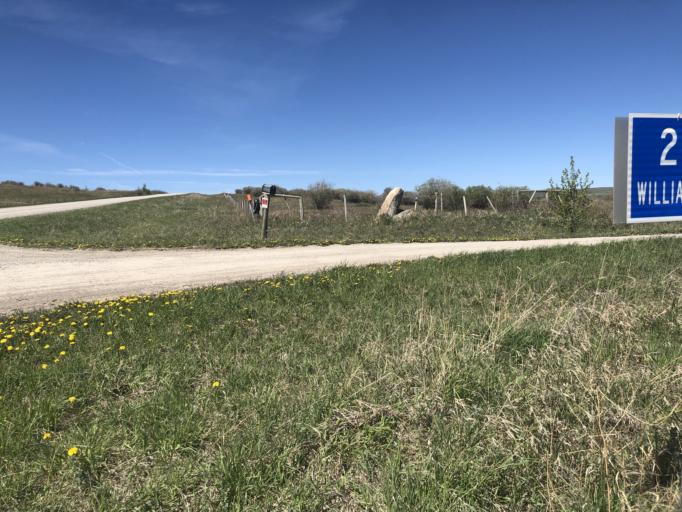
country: CA
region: Alberta
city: High River
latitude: 50.3390
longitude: -114.1393
